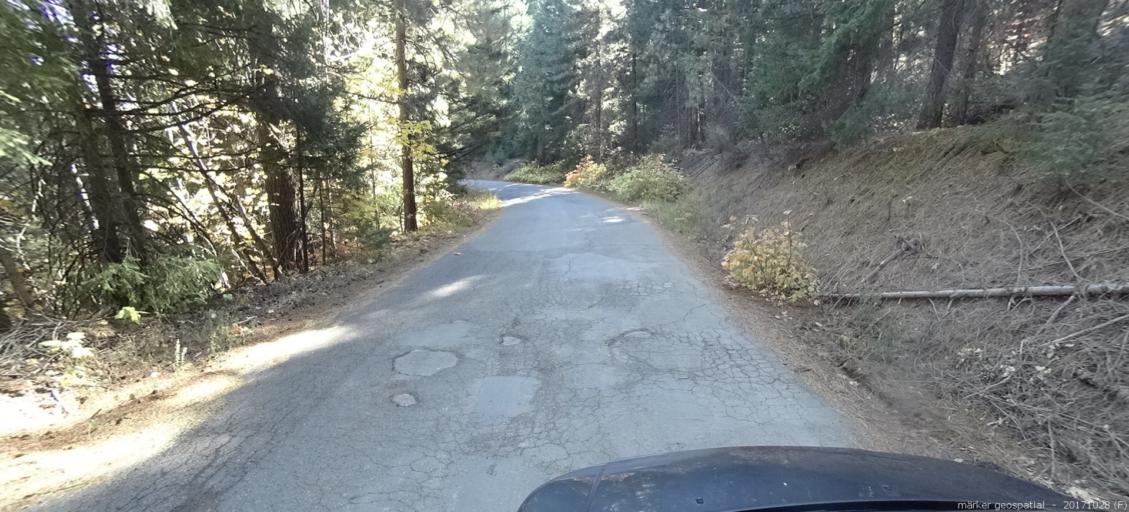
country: US
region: California
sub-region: Trinity County
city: Lewiston
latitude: 40.8220
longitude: -122.6618
